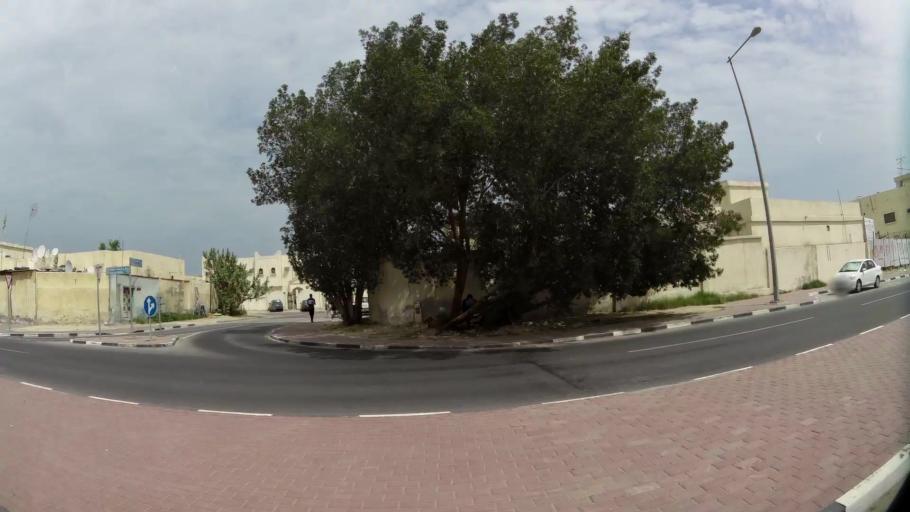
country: QA
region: Baladiyat ar Rayyan
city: Ar Rayyan
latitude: 25.3244
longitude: 51.4728
